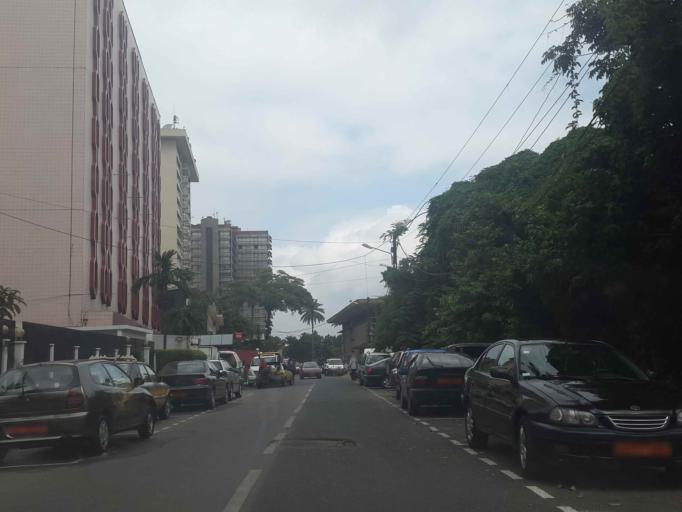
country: CM
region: Littoral
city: Douala
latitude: 4.0394
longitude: 9.6883
